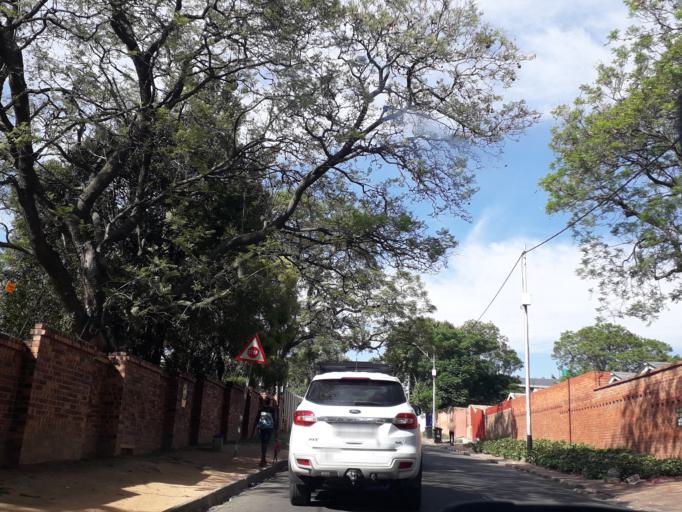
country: ZA
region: Gauteng
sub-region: City of Johannesburg Metropolitan Municipality
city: Modderfontein
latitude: -26.1286
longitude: 28.0983
